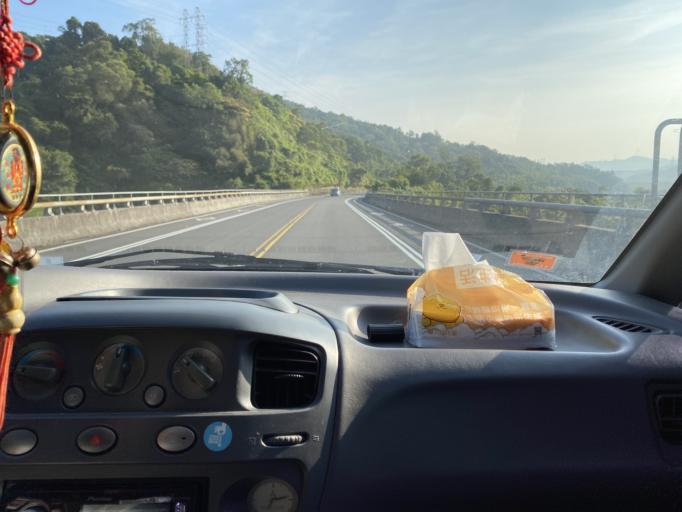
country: TW
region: Taiwan
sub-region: Keelung
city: Keelung
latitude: 25.0194
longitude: 121.8068
